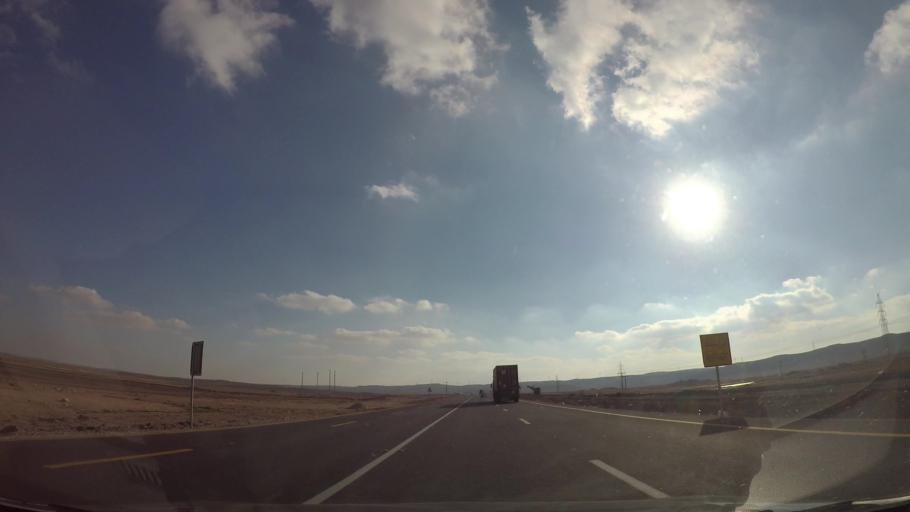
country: JO
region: Karak
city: Karak City
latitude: 31.1209
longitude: 36.0129
